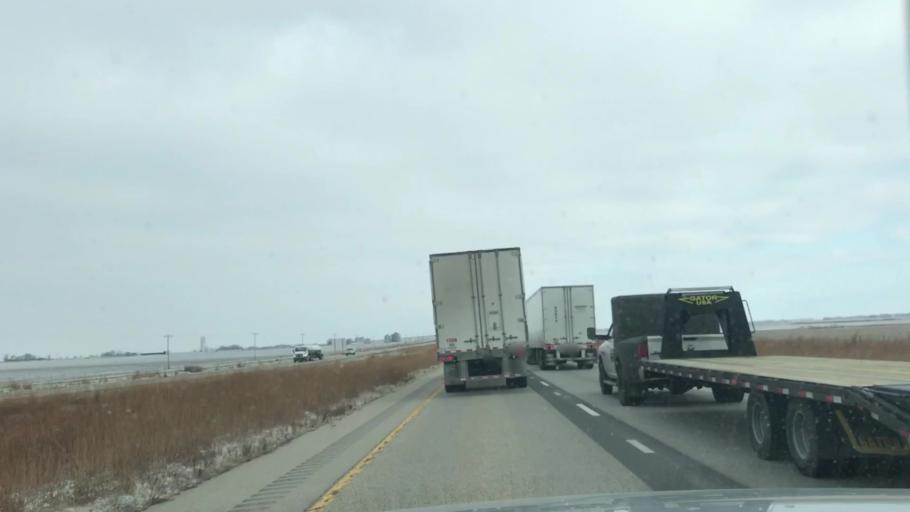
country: US
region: Illinois
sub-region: Sangamon County
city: Divernon
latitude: 39.4671
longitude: -89.6444
